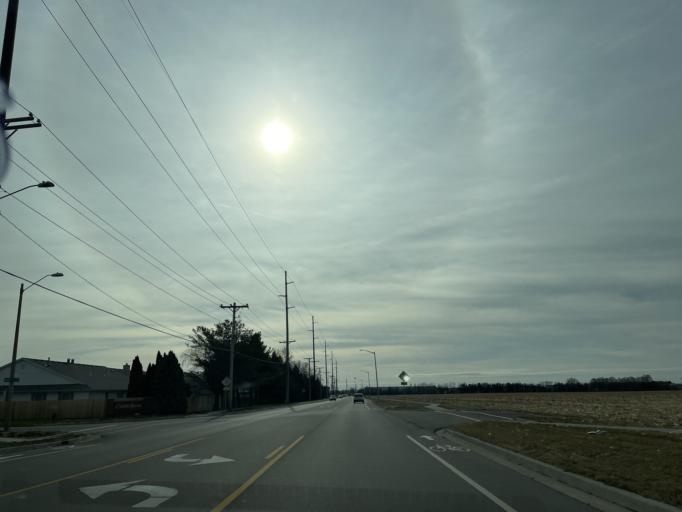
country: US
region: Illinois
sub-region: Sangamon County
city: Jerome
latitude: 39.7646
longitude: -89.7346
